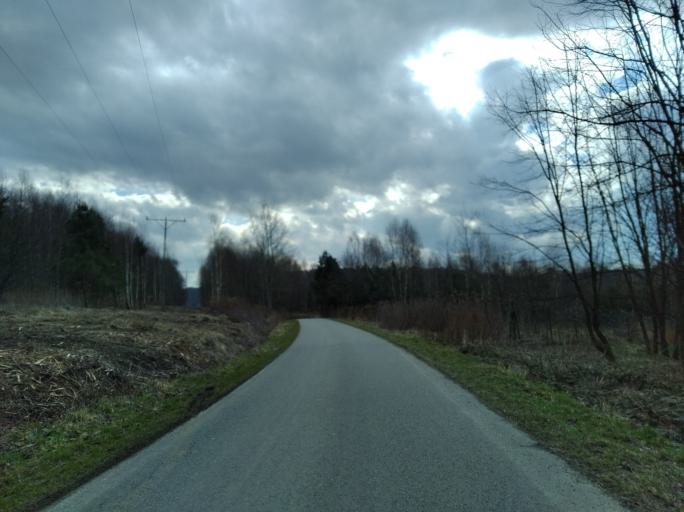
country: PL
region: Subcarpathian Voivodeship
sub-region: Powiat strzyzowski
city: Wysoka Strzyzowska
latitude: 49.7961
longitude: 21.7281
